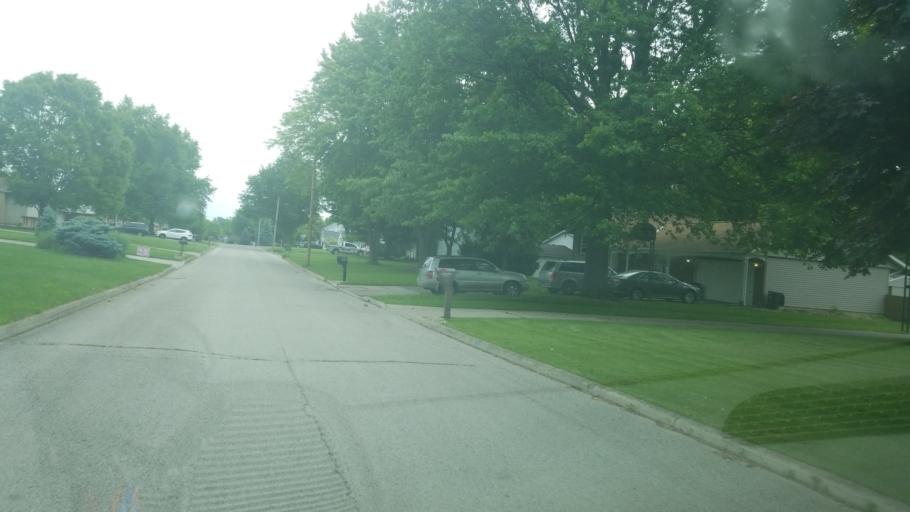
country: US
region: Ohio
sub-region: Crawford County
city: Bucyrus
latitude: 40.7936
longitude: -82.9892
